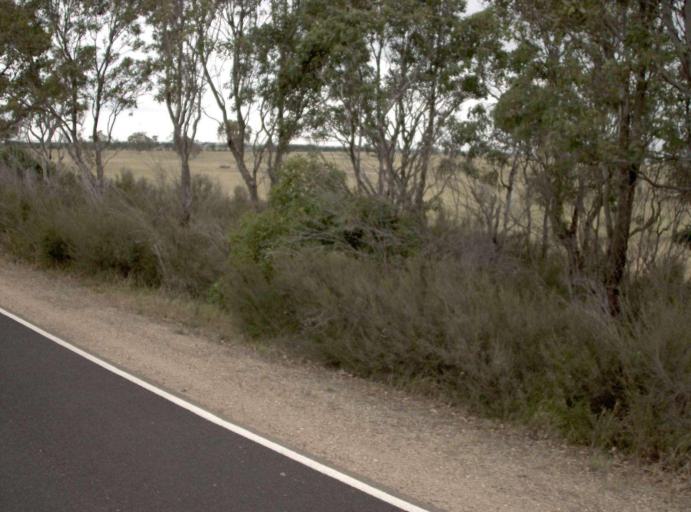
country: AU
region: Victoria
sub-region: Wellington
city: Sale
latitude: -37.9961
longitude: 147.2083
